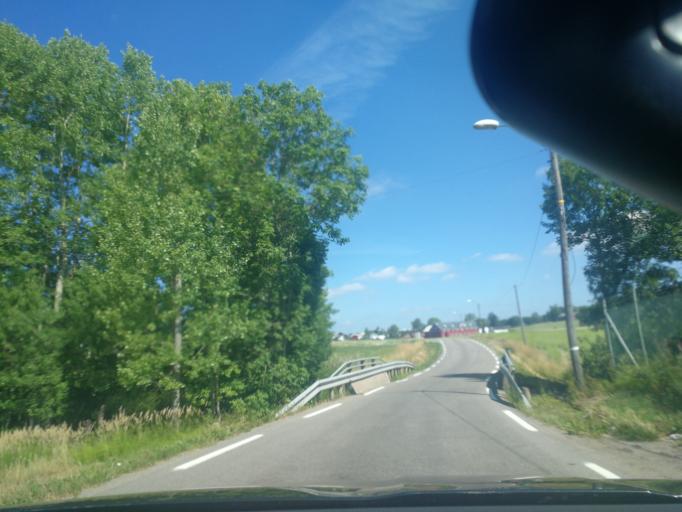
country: NO
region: Vestfold
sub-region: Stokke
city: Stokke
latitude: 59.2133
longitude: 10.2944
